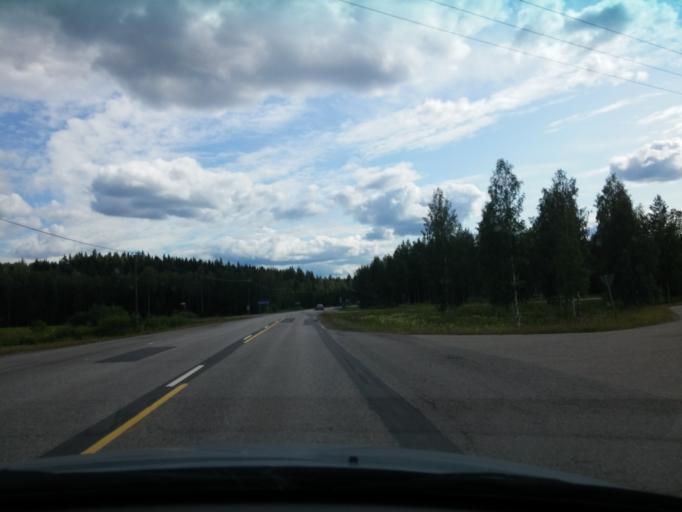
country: FI
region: Central Finland
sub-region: Keuruu
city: Multia
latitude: 62.3598
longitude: 24.7402
